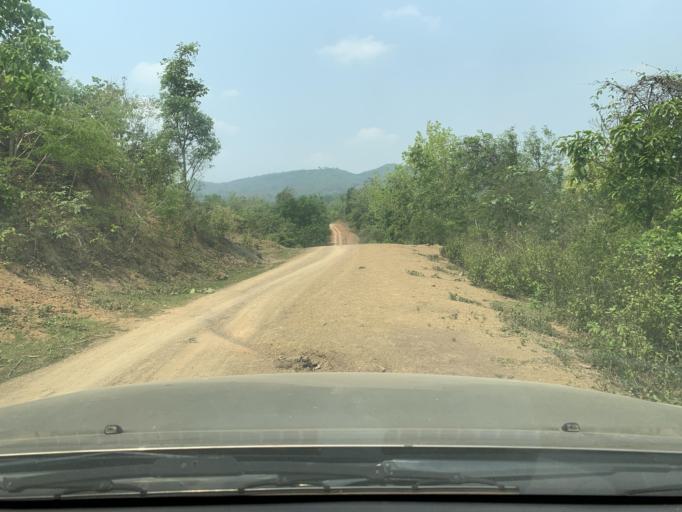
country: LA
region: Louangphabang
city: Louangphabang
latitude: 19.9377
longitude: 102.1361
